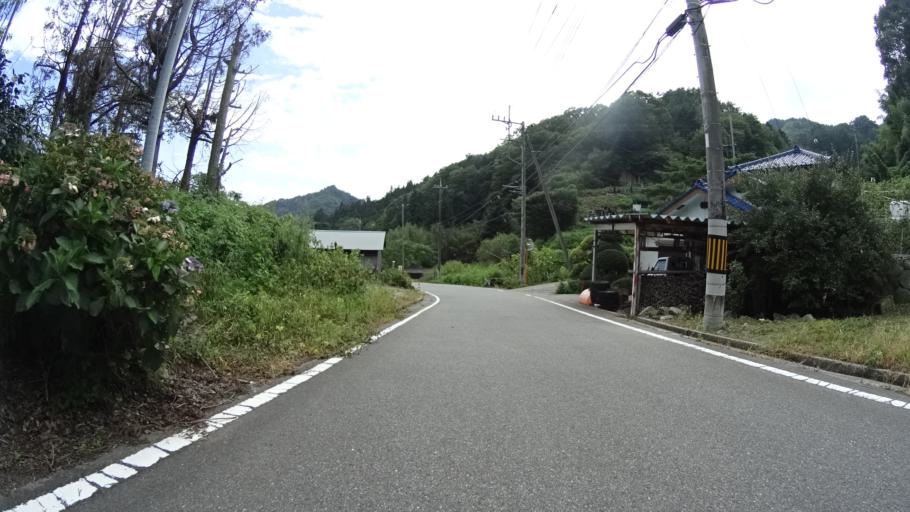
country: JP
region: Yamanashi
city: Nirasaki
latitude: 35.7705
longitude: 138.5328
